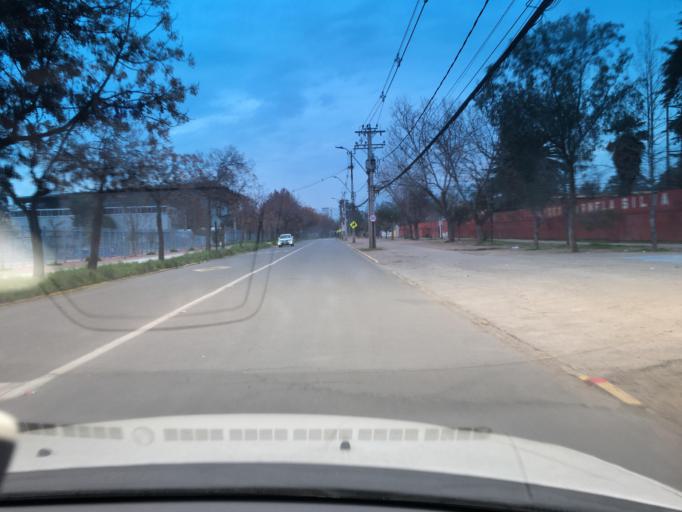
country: CL
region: Santiago Metropolitan
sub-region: Provincia de Santiago
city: Villa Presidente Frei, Nunoa, Santiago, Chile
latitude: -33.4680
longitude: -70.6066
